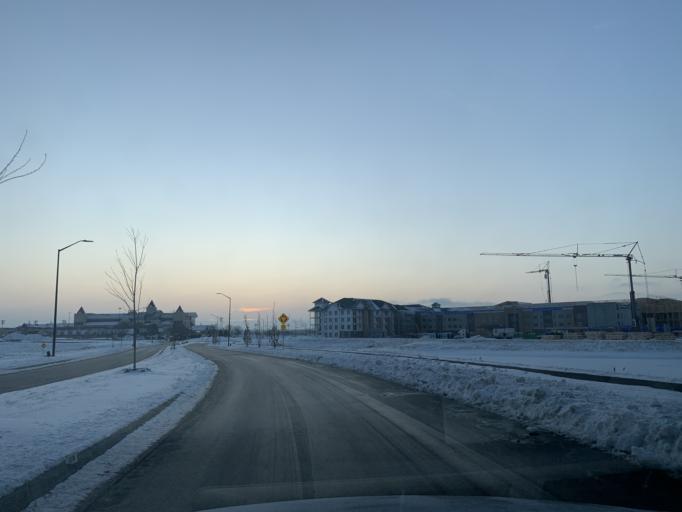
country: US
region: Minnesota
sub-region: Scott County
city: Shakopee
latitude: 44.7929
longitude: -93.4898
